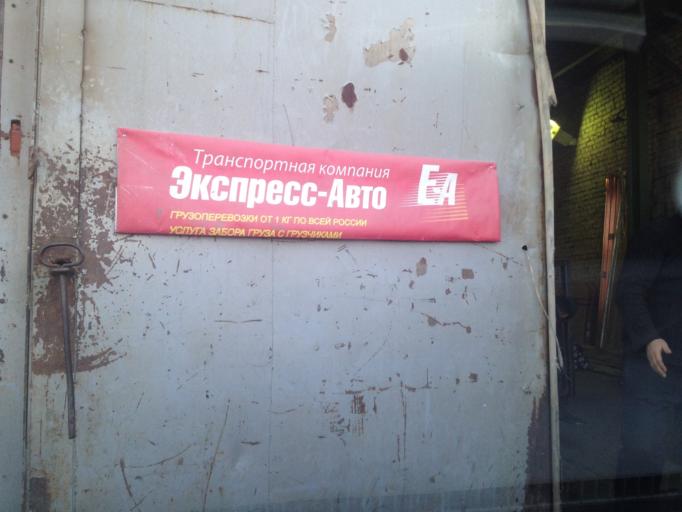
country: RU
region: Sverdlovsk
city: Sovkhoznyy
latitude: 56.8105
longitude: 60.5396
